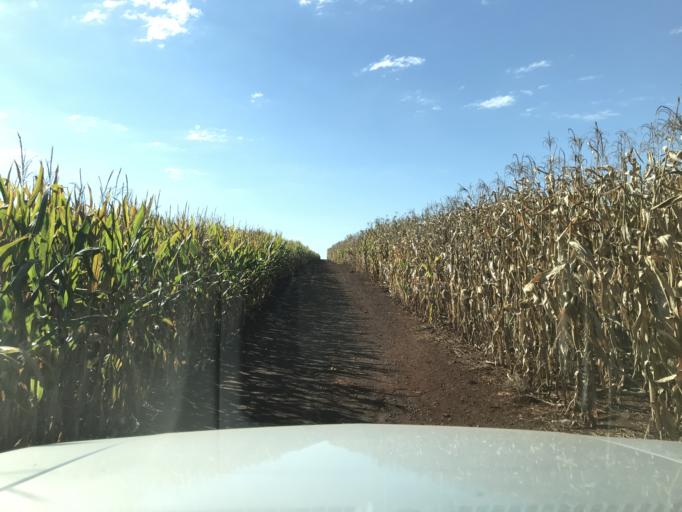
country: BR
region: Parana
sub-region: Palotina
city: Palotina
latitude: -24.2638
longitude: -53.8134
